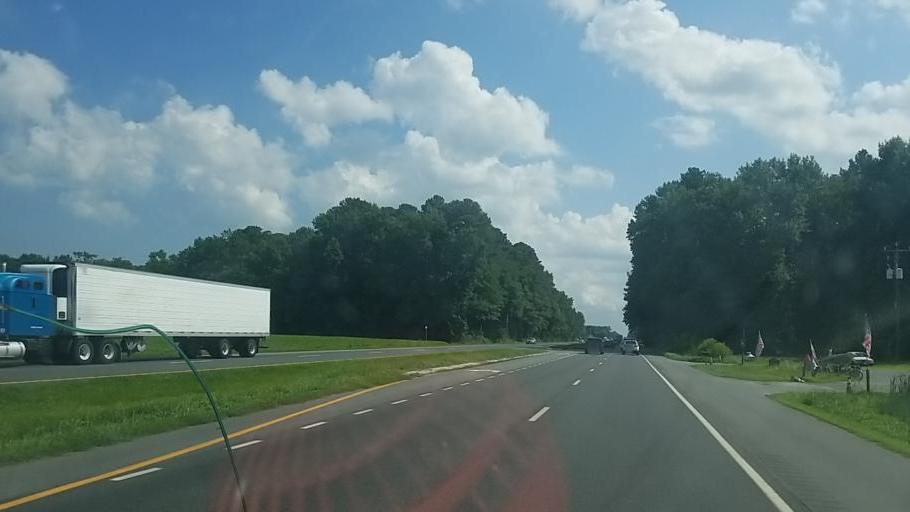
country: US
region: Delaware
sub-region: Sussex County
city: Selbyville
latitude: 38.5071
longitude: -75.2379
